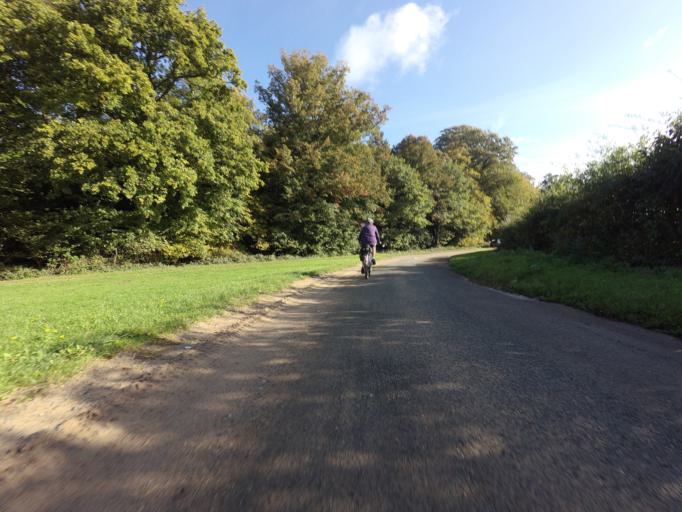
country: GB
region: England
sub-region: Norfolk
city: Dersingham
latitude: 52.8200
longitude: 0.6409
